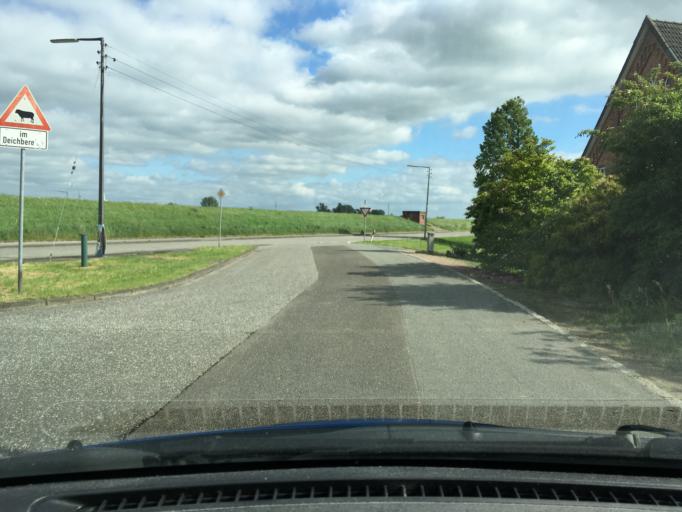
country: DE
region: Hamburg
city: Rothenburgsort
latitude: 53.4738
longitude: 10.0599
